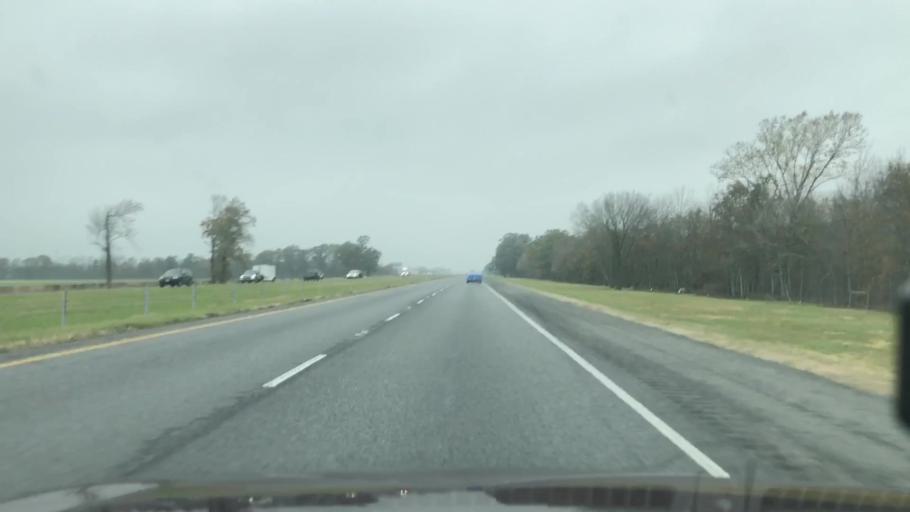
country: US
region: Louisiana
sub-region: Ouachita Parish
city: Lakeshore
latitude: 32.4905
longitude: -92.0066
